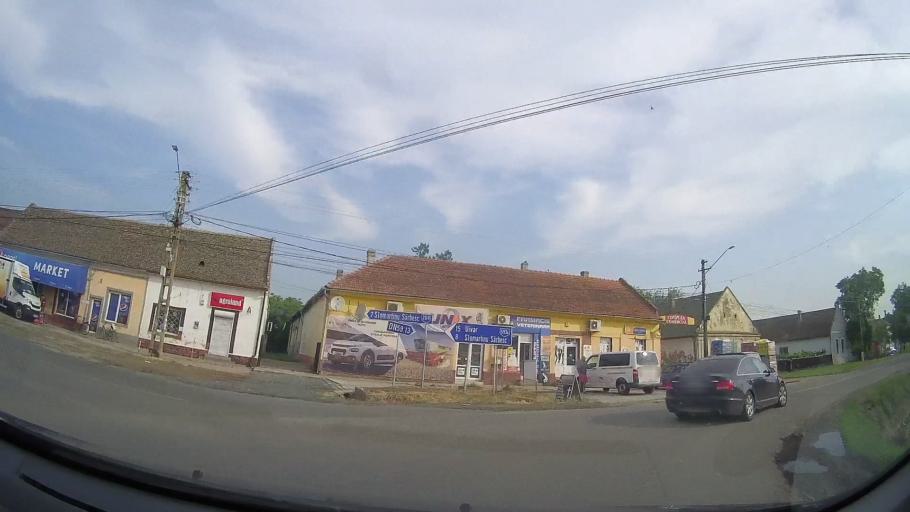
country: RO
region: Timis
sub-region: Comuna Peciu Nou
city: Peciu Nou
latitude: 45.6033
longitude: 21.0537
